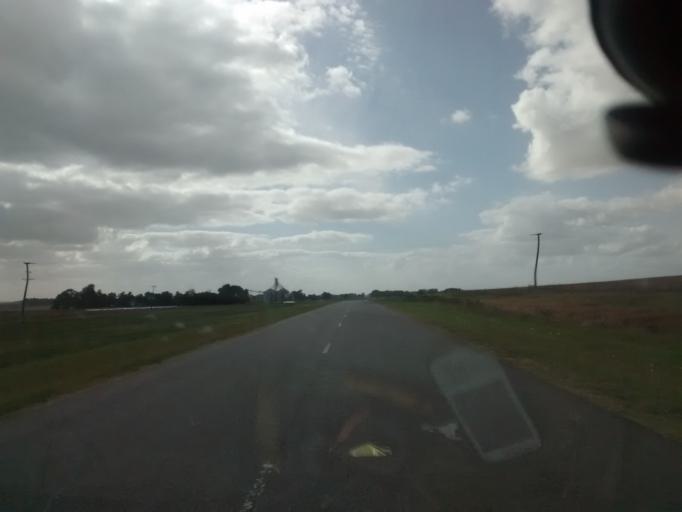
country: AR
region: Buenos Aires
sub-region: Partido de Loberia
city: Loberia
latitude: -37.6608
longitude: -58.7357
